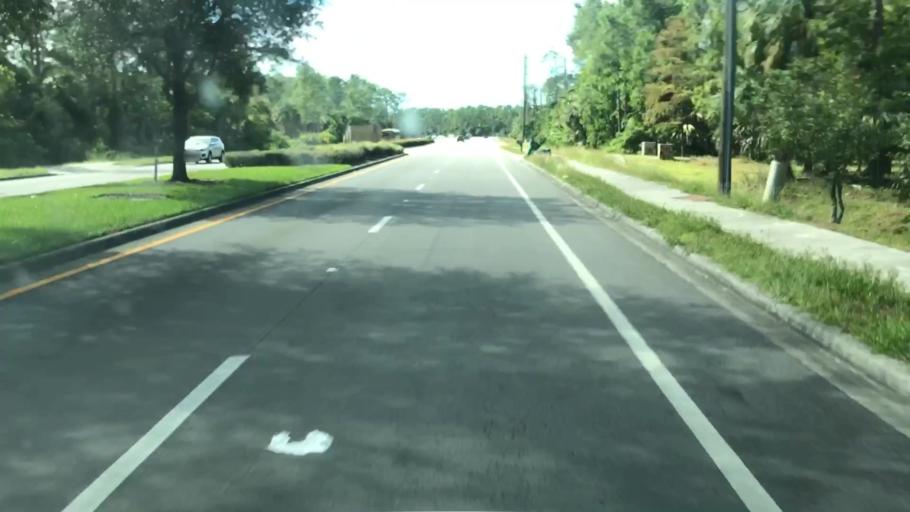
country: US
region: Florida
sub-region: Collier County
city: Vineyards
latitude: 26.2290
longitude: -81.6832
